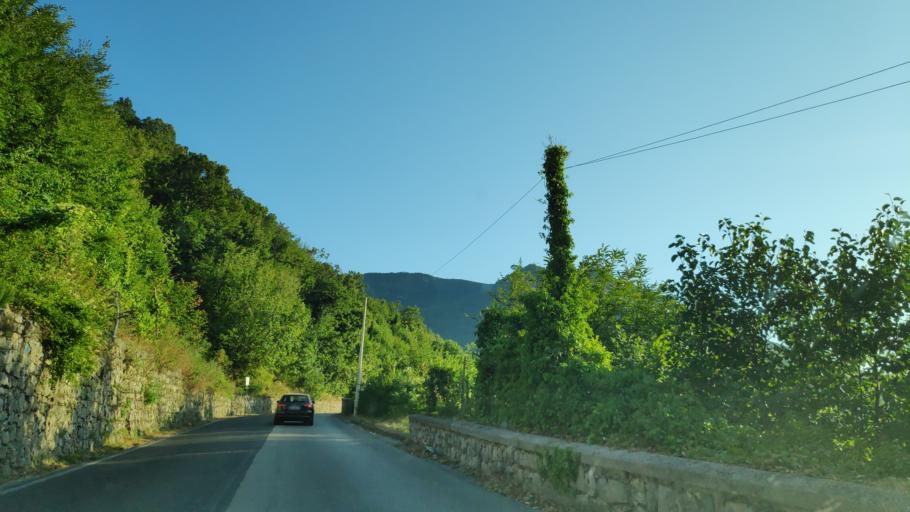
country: IT
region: Campania
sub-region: Provincia di Salerno
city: Corbara
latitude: 40.7209
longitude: 14.6009
